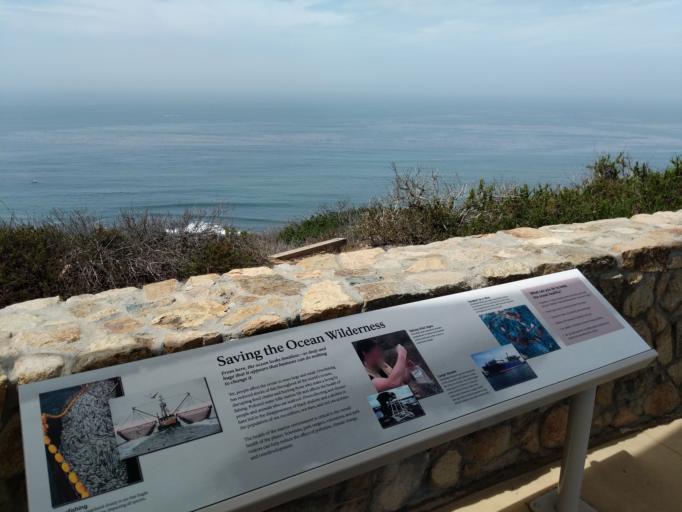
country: US
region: California
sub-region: San Diego County
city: Coronado
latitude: 32.6707
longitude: -117.2414
